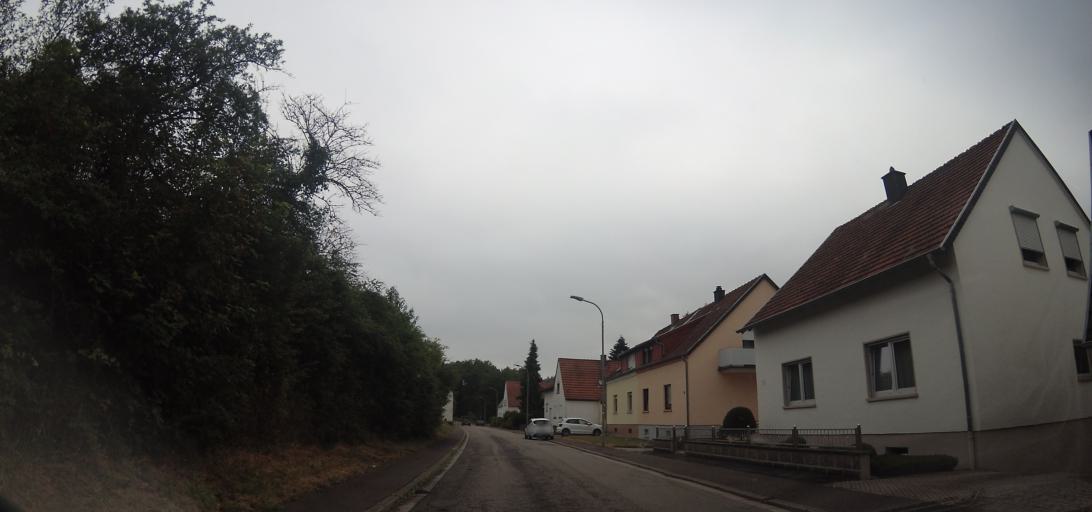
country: DE
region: Saarland
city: Homburg
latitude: 49.3062
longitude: 7.3734
